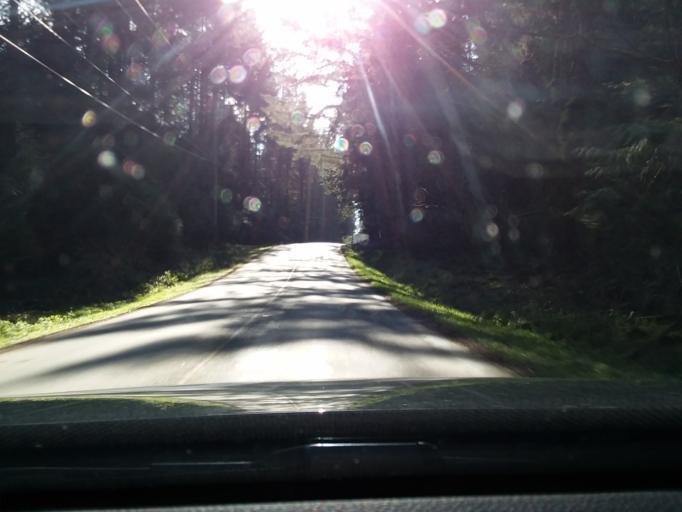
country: CA
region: British Columbia
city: North Saanich
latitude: 48.9189
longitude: -123.4360
